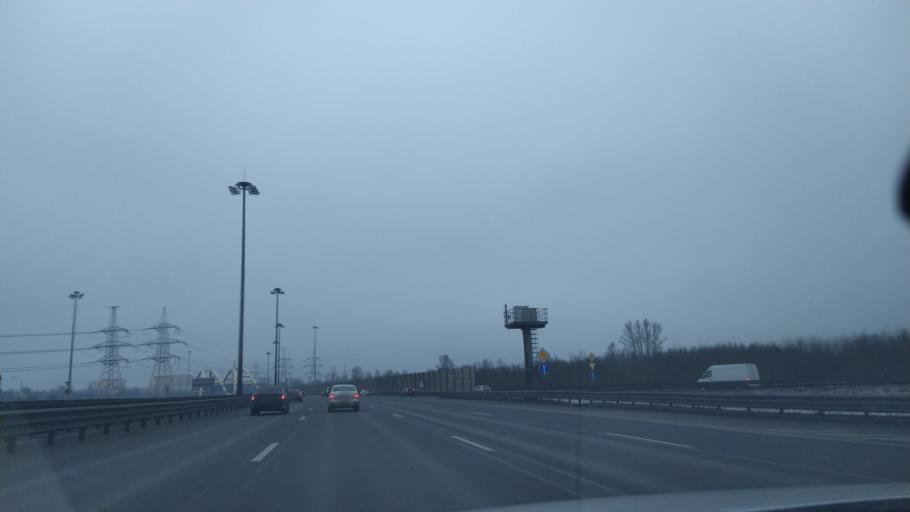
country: RU
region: St.-Petersburg
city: Krasnogvargeisky
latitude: 59.9896
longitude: 30.4841
